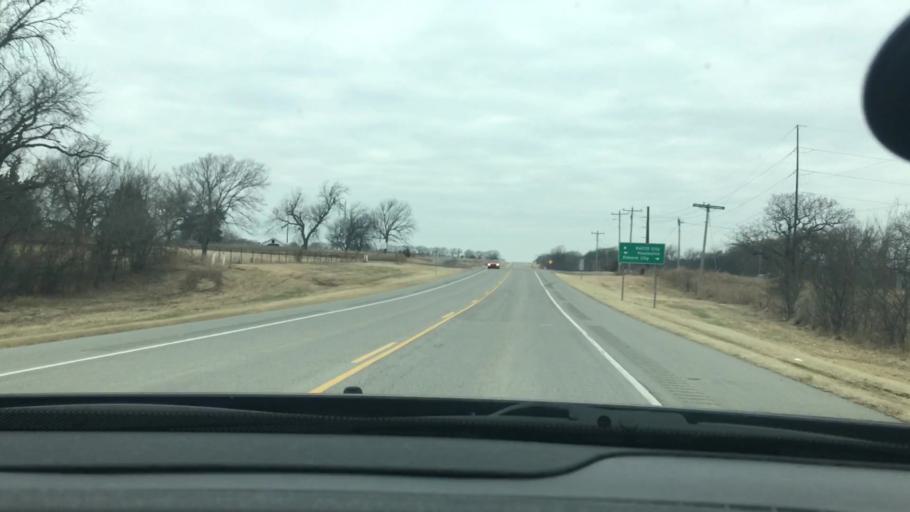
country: US
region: Oklahoma
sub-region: Carter County
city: Healdton
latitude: 34.4924
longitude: -97.4031
